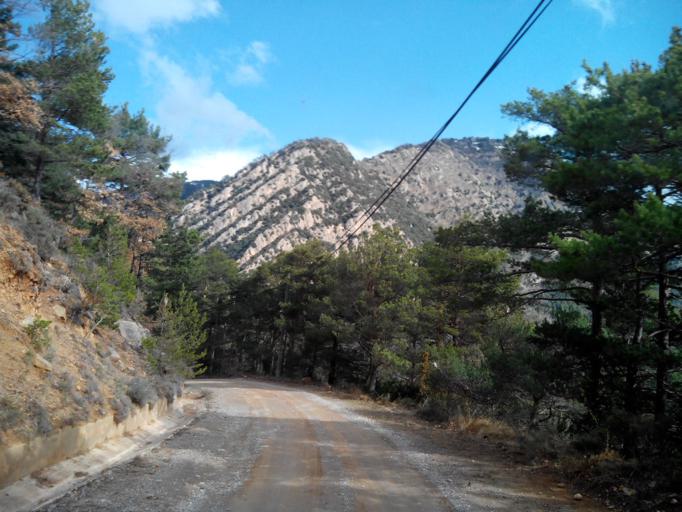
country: ES
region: Catalonia
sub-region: Provincia de Barcelona
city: Vilada
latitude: 42.1650
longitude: 1.9318
